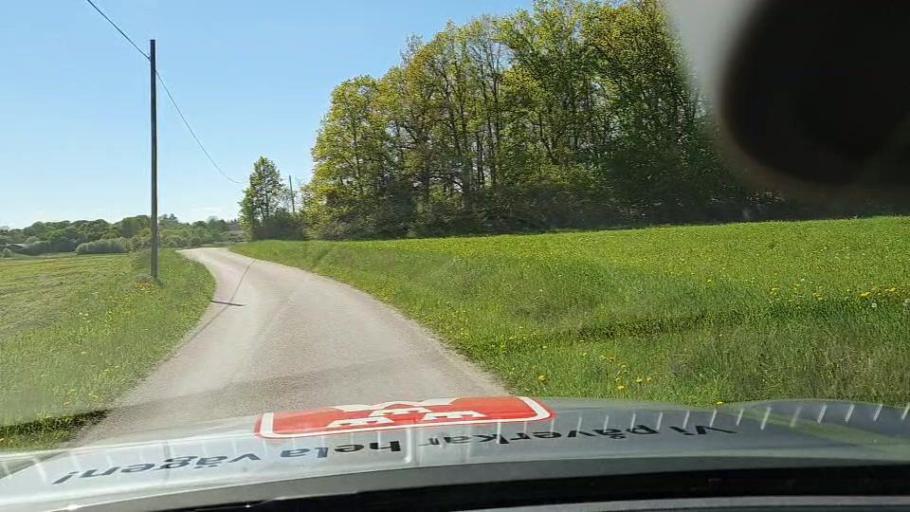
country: SE
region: Soedermanland
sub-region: Strangnas Kommun
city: Strangnas
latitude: 59.4563
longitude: 16.8859
